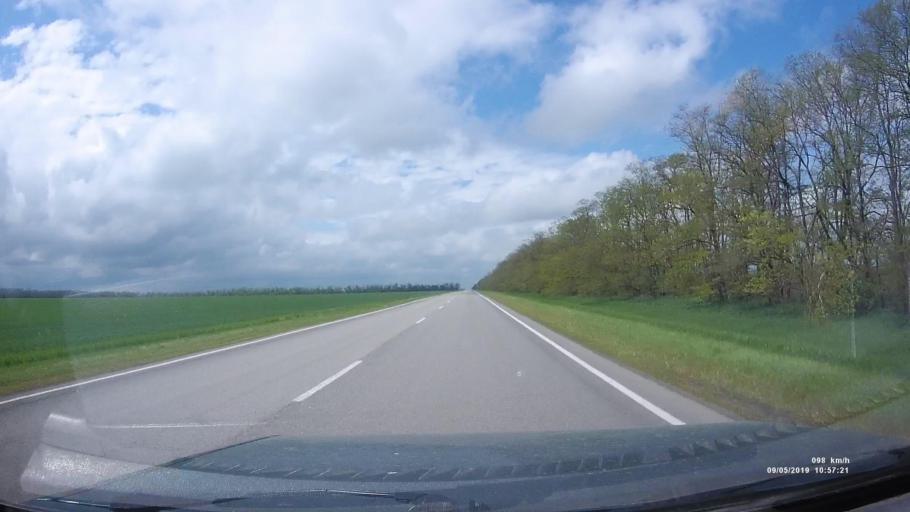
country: RU
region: Rostov
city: Peshkovo
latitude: 46.8658
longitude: 39.2807
